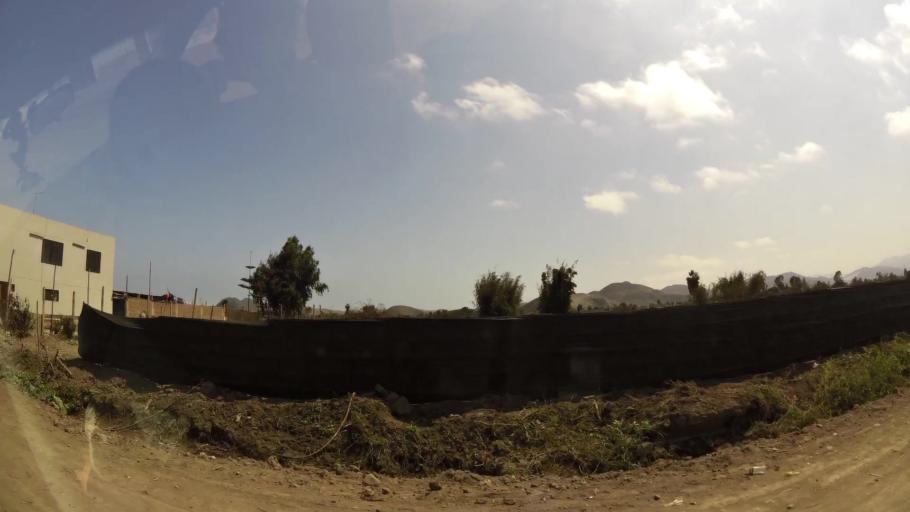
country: PE
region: Lima
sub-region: Provincia de Canete
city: Mala
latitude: -12.6713
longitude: -76.6457
